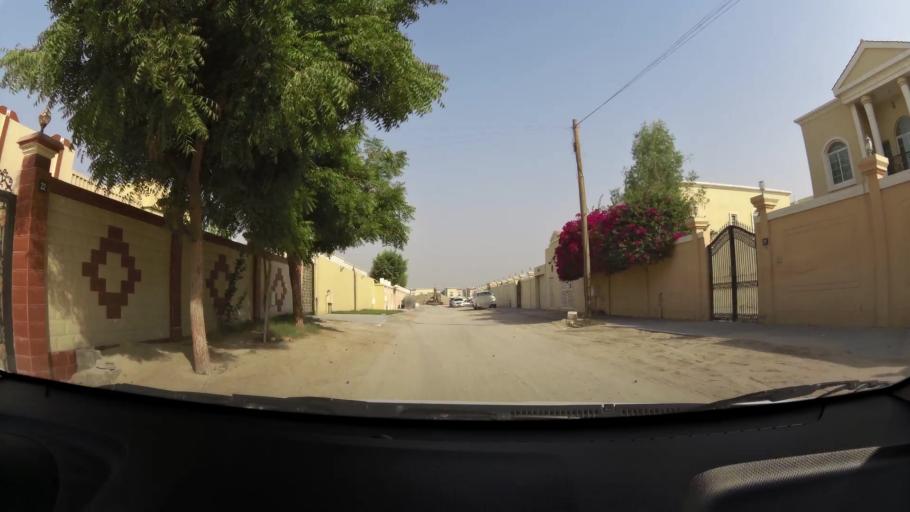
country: AE
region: Ajman
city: Ajman
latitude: 25.3794
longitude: 55.4225
